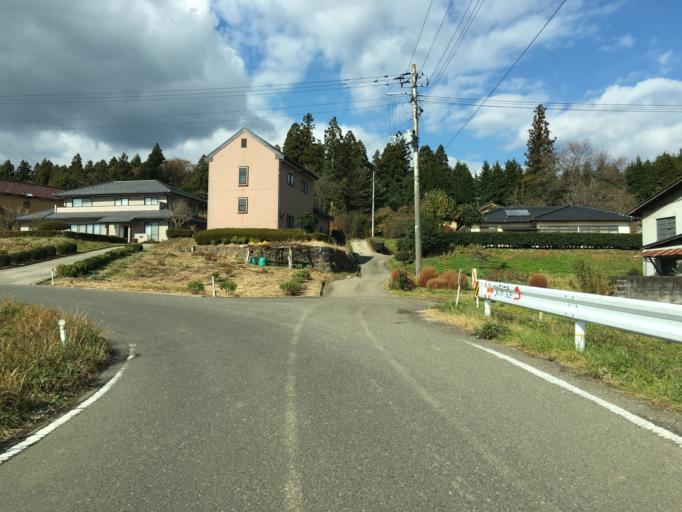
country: JP
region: Fukushima
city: Nihommatsu
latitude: 37.6314
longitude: 140.4790
